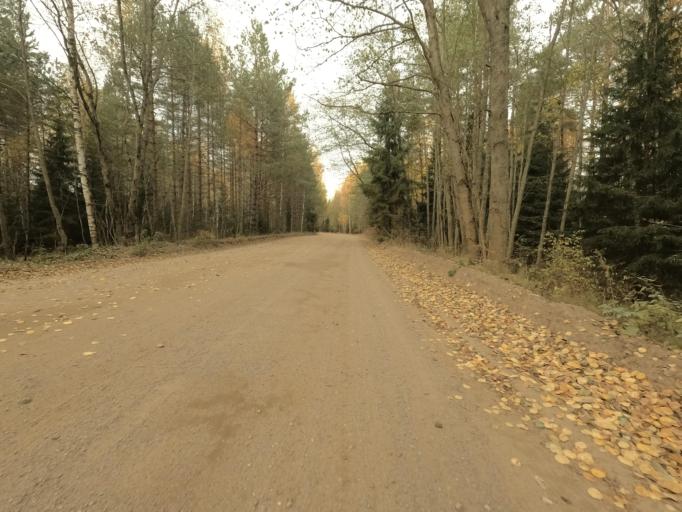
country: RU
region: Leningrad
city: Priladozhskiy
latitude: 59.6859
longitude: 31.3620
